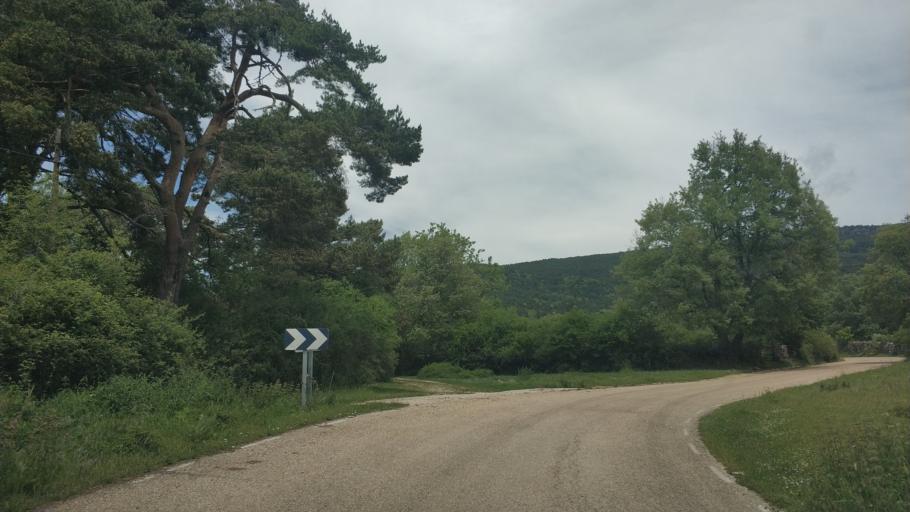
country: ES
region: Castille and Leon
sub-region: Provincia de Soria
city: Vinuesa
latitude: 41.9705
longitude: -2.7806
